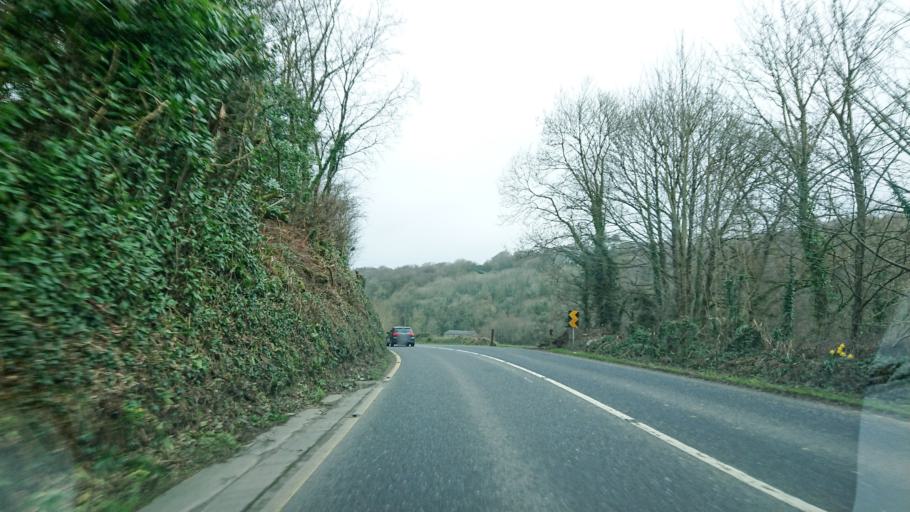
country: IE
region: Munster
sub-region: County Cork
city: Bandon
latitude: 51.7667
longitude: -8.6713
